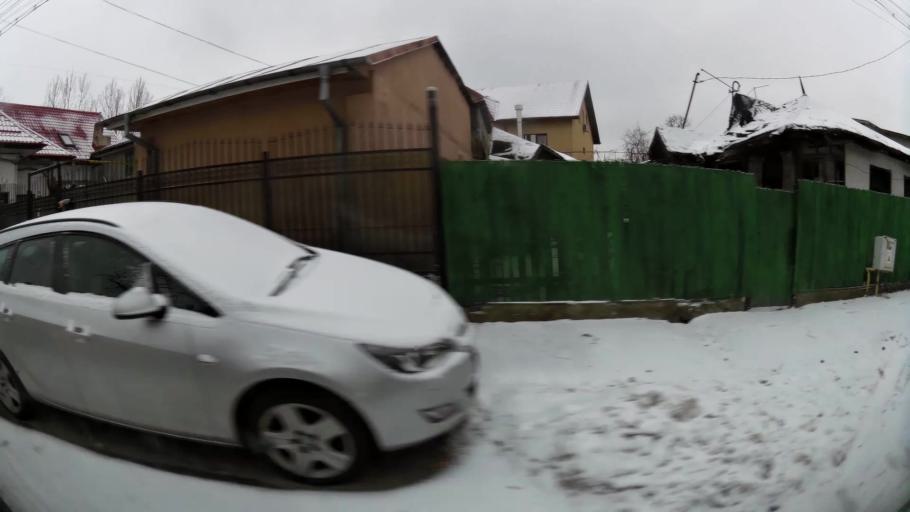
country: RO
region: Prahova
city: Ploiesti
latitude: 44.9367
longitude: 26.0420
